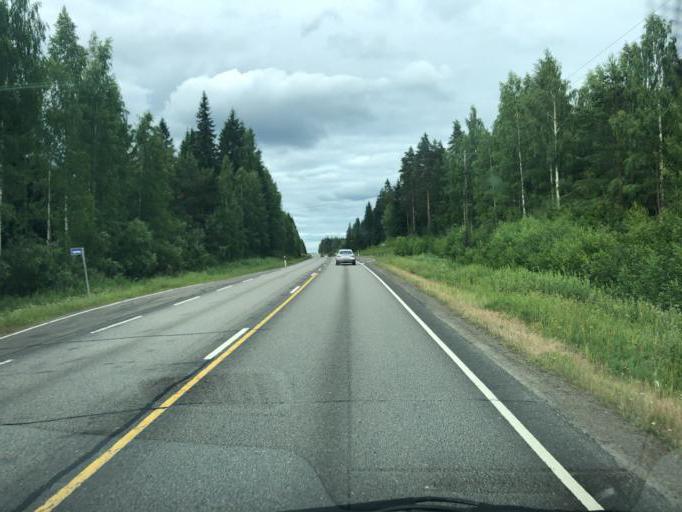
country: FI
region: Kymenlaakso
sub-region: Kouvola
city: Kouvola
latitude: 60.9843
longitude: 26.9136
